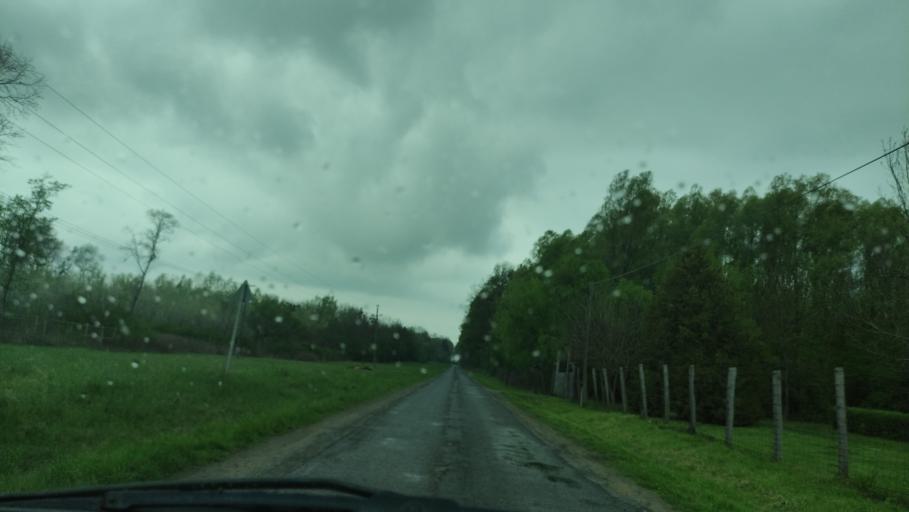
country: HU
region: Baranya
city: Mohacs
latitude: 45.9300
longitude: 18.7242
